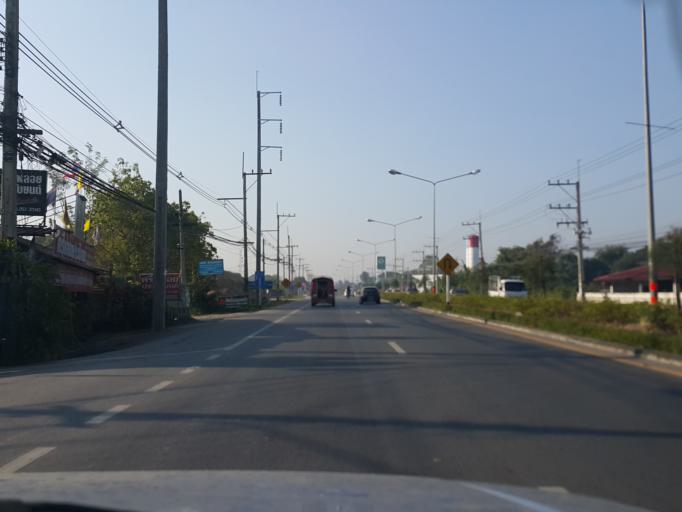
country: TH
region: Chiang Mai
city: San Pa Tong
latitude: 18.6370
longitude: 98.8992
